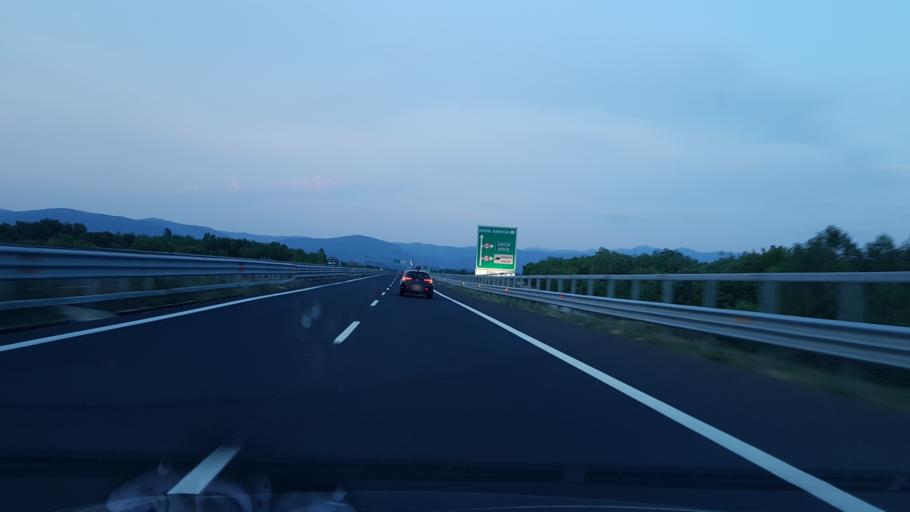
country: IT
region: Friuli Venezia Giulia
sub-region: Provincia di Gorizia
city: Savogna d'Isonzo
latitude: 45.9065
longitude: 13.5894
